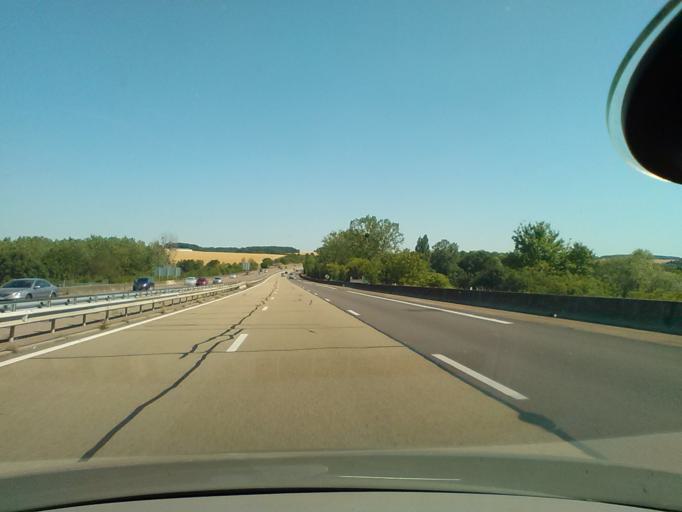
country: FR
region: Bourgogne
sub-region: Departement de l'Yonne
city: Saint-Julien-du-Sault
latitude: 47.9499
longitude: 3.2313
